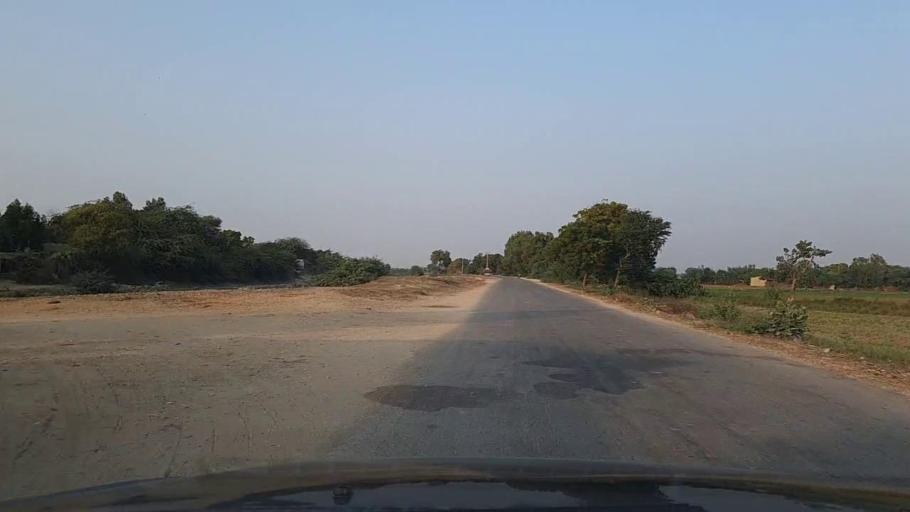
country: PK
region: Sindh
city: Mirpur Sakro
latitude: 24.5320
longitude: 67.8299
